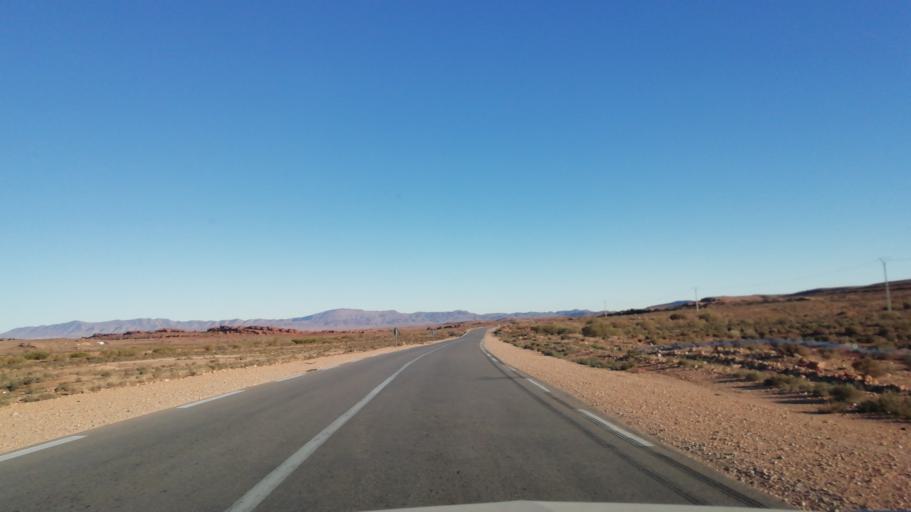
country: DZ
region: El Bayadh
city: El Abiodh Sidi Cheikh
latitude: 33.1746
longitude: 0.4514
